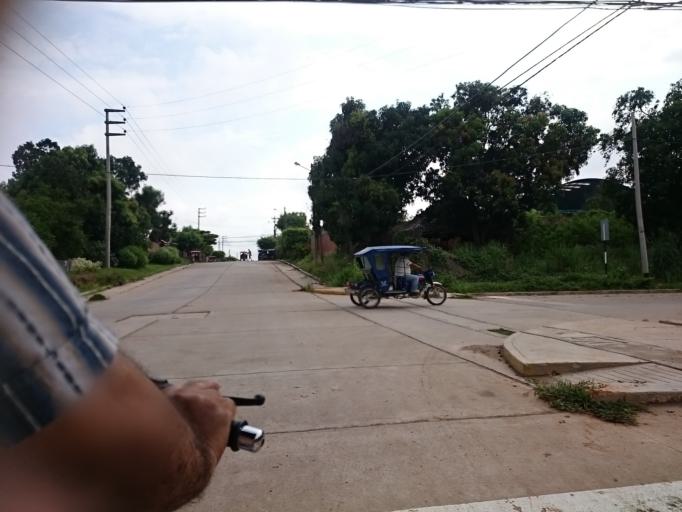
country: PE
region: Ucayali
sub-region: Provincia de Coronel Portillo
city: Puerto Callao
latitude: -8.3625
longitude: -74.5735
